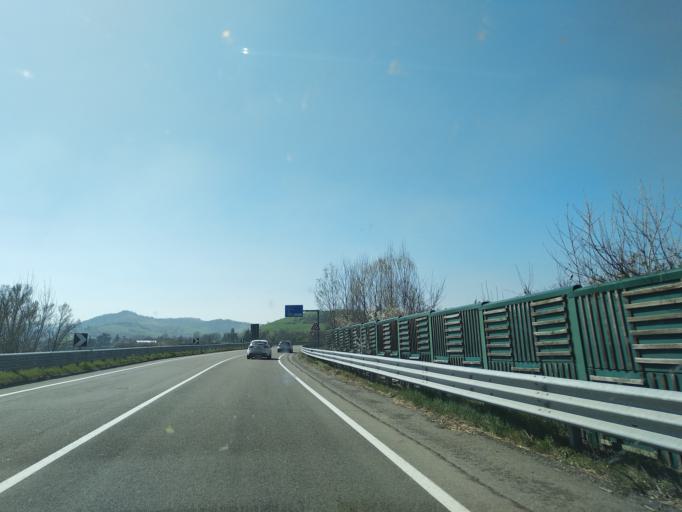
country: IT
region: Emilia-Romagna
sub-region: Provincia di Reggio Emilia
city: Puianello
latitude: 44.6186
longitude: 10.5594
